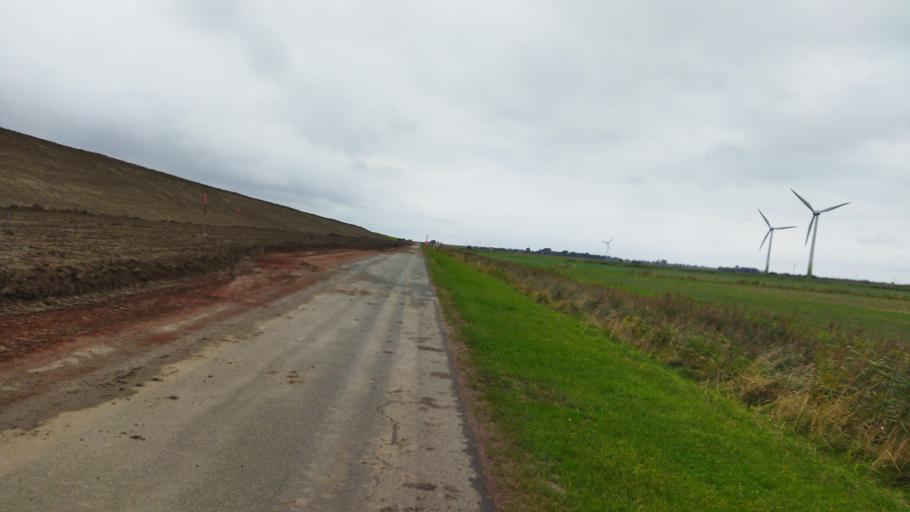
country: NL
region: Groningen
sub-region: Gemeente Delfzijl
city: Delfzijl
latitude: 53.4408
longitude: 7.0198
